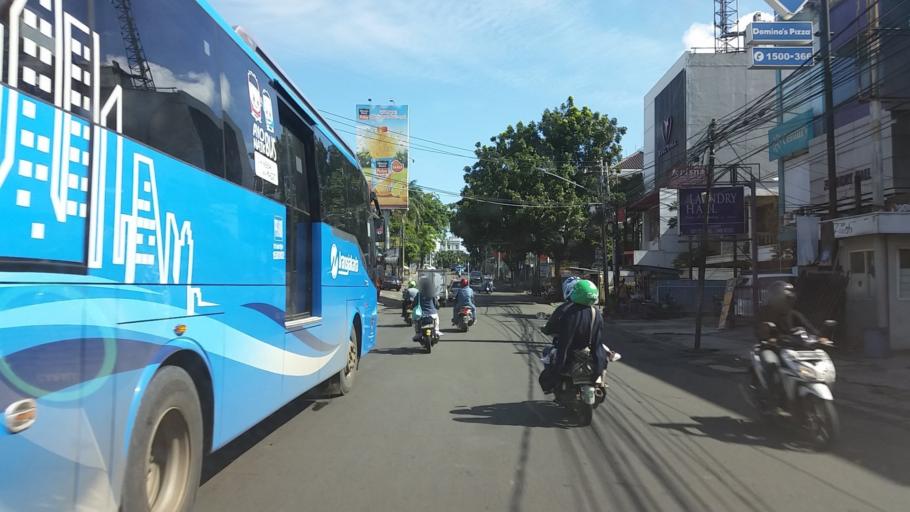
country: ID
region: Jakarta Raya
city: Jakarta
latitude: -6.2576
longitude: 106.7897
